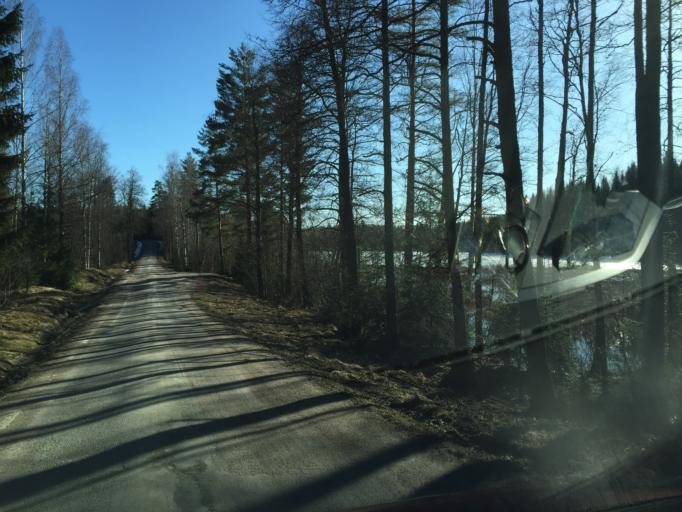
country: SE
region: Soedermanland
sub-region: Vingakers Kommun
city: Vingaker
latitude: 58.9624
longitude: 15.6568
